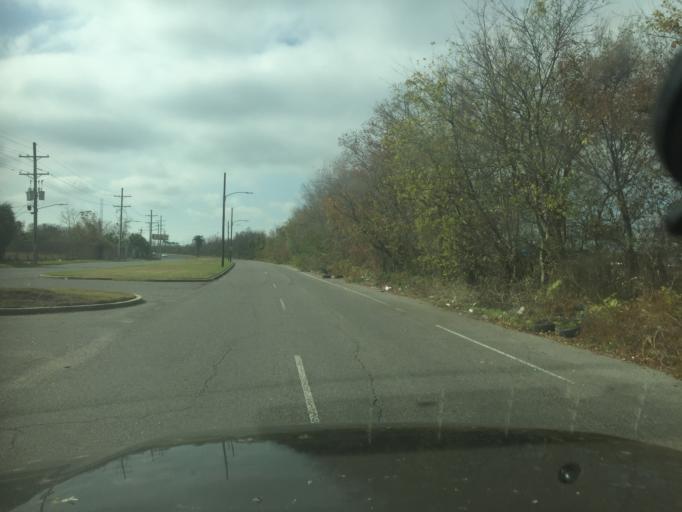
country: US
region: Louisiana
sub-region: Saint Bernard Parish
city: Arabi
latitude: 30.0013
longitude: -90.0377
